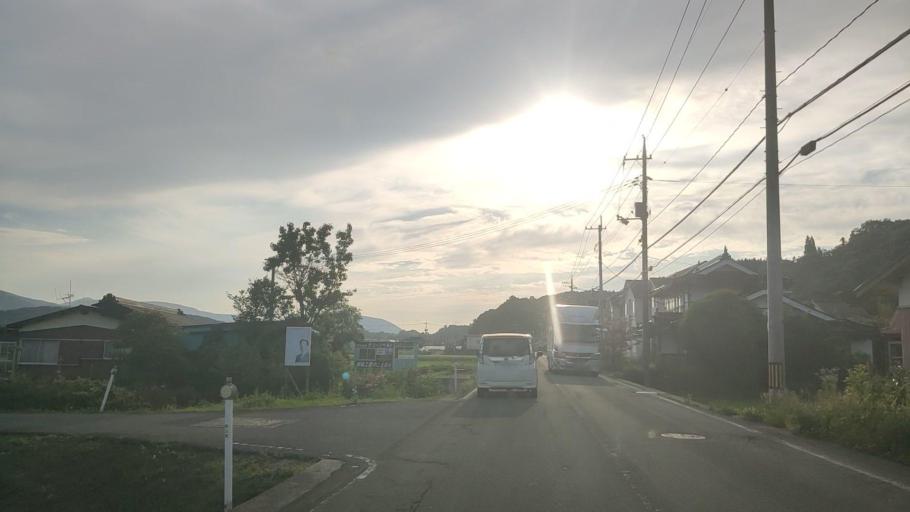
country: JP
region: Tottori
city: Kurayoshi
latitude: 35.2803
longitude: 133.6706
